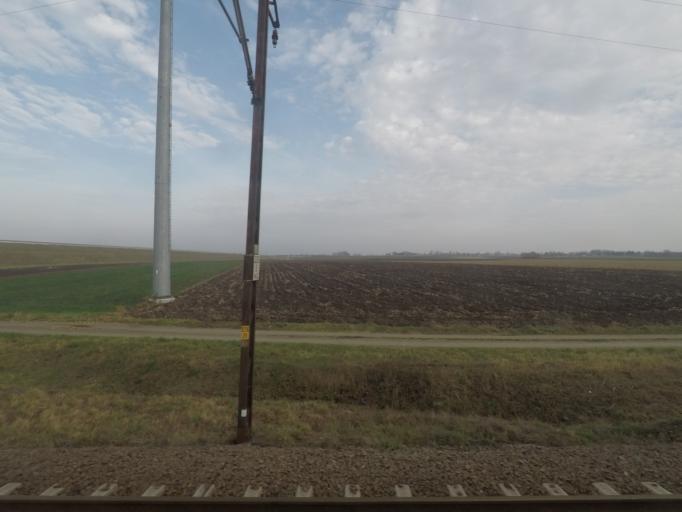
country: PL
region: Subcarpathian Voivodeship
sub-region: Powiat jaroslawski
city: Sosnica
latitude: 49.9121
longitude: 22.8466
